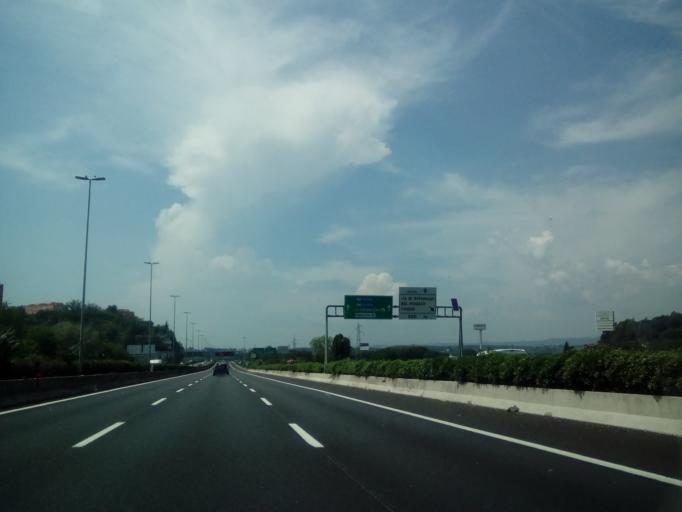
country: IT
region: Latium
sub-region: Citta metropolitana di Roma Capitale
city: Rome
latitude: 41.9850
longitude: 12.5216
